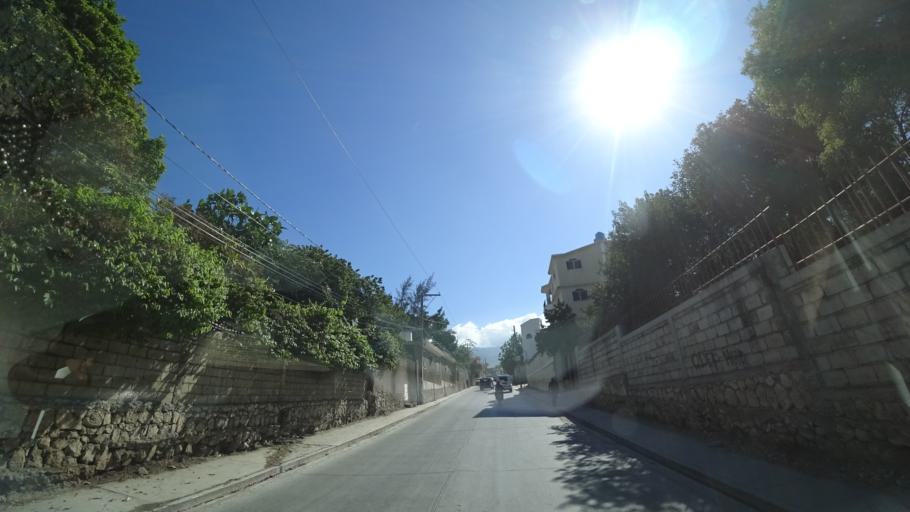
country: HT
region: Ouest
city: Delmas 73
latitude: 18.5437
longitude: -72.2867
